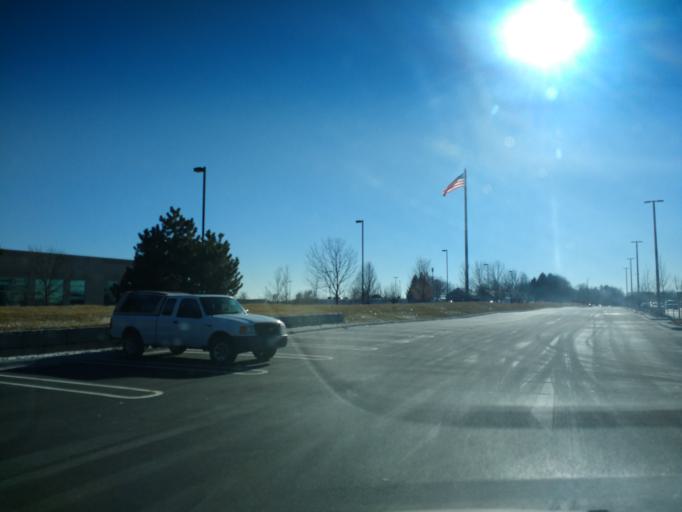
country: US
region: Iowa
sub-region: Scott County
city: Bettendorf
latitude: 41.5776
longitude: -90.5330
